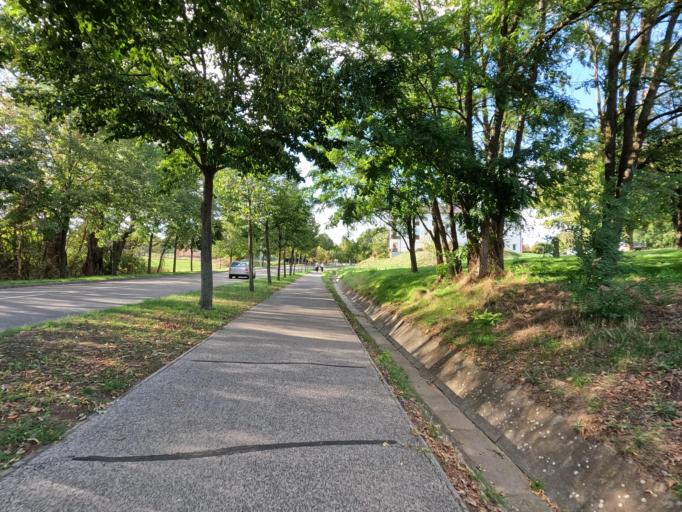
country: HU
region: Tolna
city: Paks
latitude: 46.6113
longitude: 18.8383
